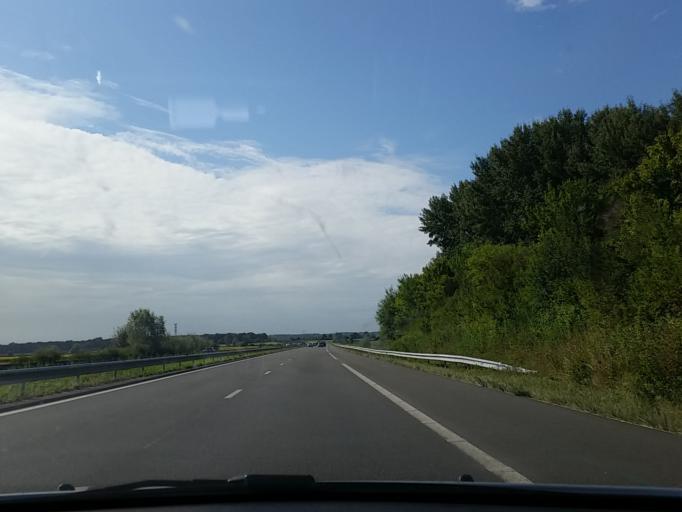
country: FR
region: Centre
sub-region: Departement du Cher
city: Chateauneuf-sur-Cher
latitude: 46.8183
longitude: 2.4128
